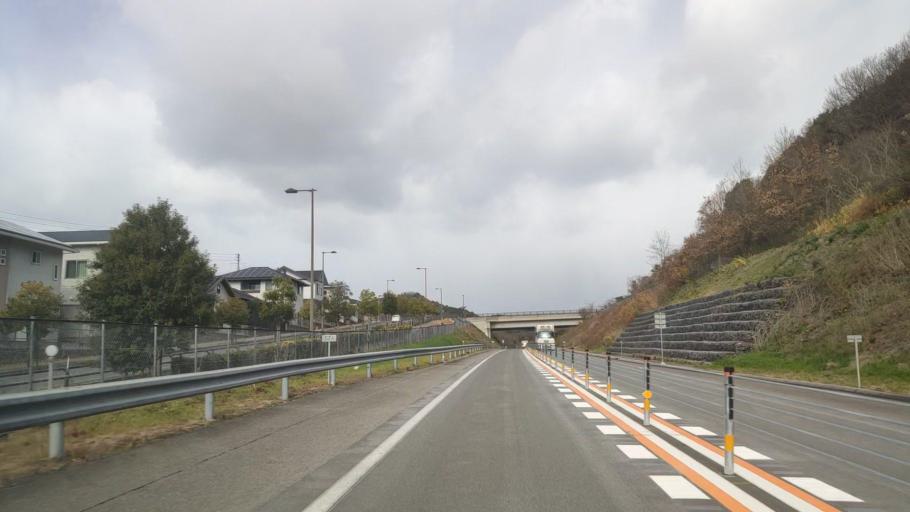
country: JP
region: Ehime
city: Hojo
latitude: 34.0685
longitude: 132.9738
